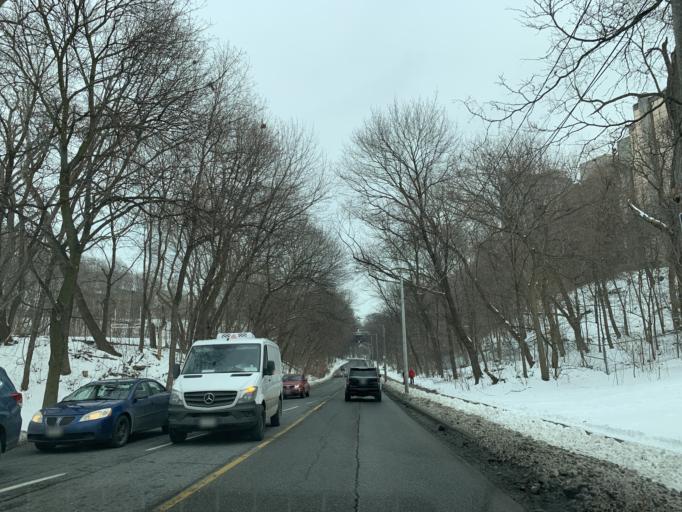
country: CA
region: Ontario
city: Toronto
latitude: 43.6735
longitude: -79.3837
